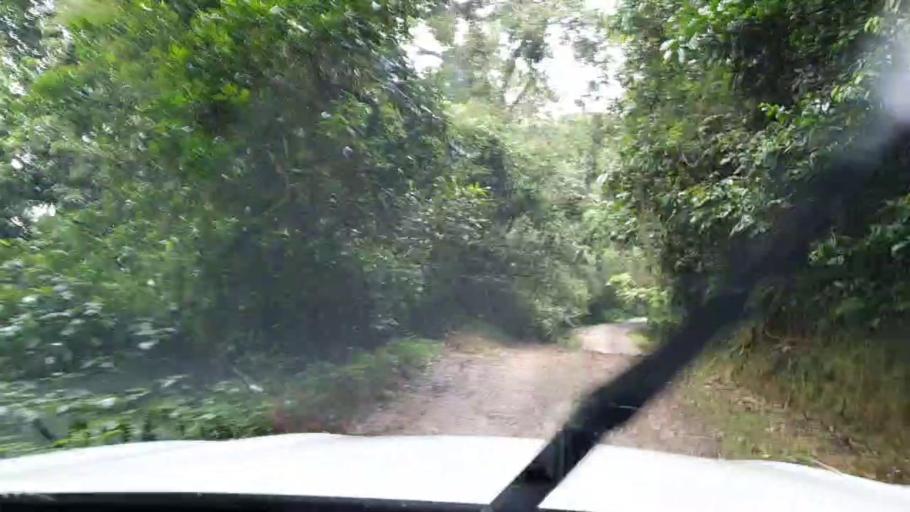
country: RW
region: Western Province
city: Cyangugu
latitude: -2.5577
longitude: 28.9806
